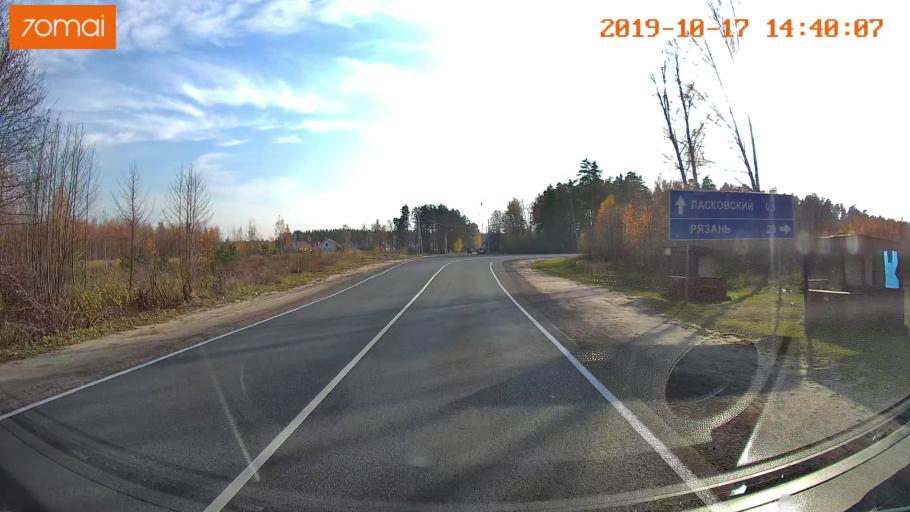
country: RU
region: Rjazan
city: Solotcha
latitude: 54.8568
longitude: 39.9612
